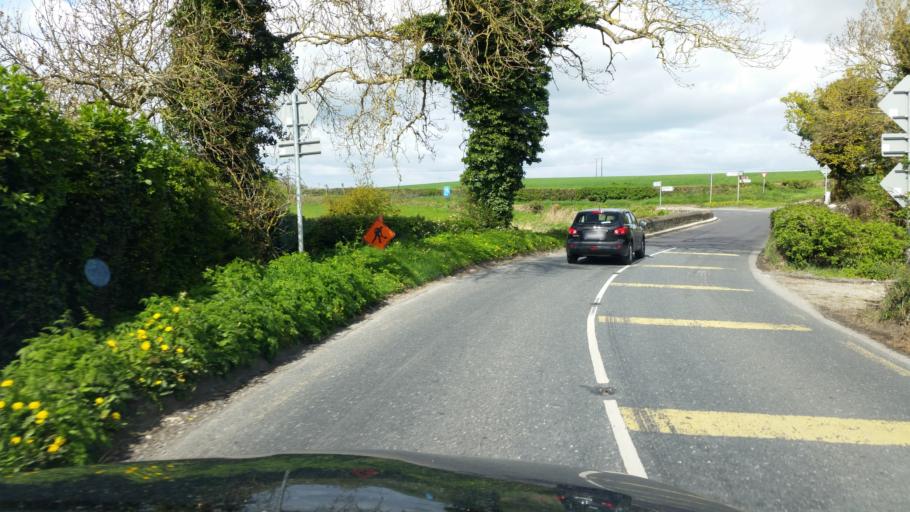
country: IE
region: Leinster
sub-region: An Mhi
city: Ashbourne
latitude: 53.4943
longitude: -6.3719
